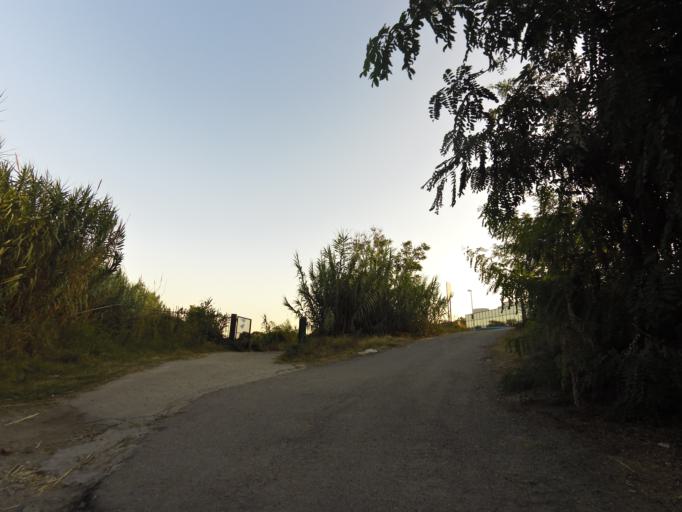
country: IT
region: Calabria
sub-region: Provincia di Reggio Calabria
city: Monasterace Marina
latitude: 38.4507
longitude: 16.5796
